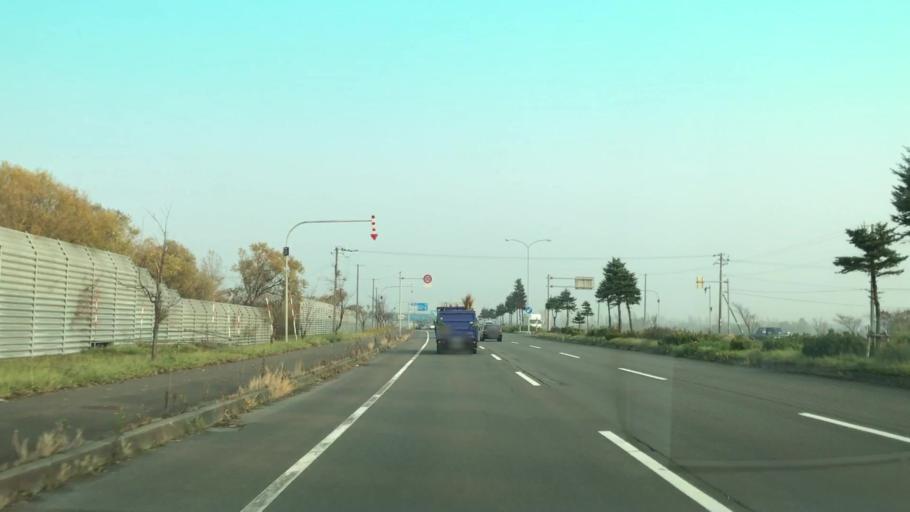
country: JP
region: Hokkaido
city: Ishikari
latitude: 43.1742
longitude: 141.3484
